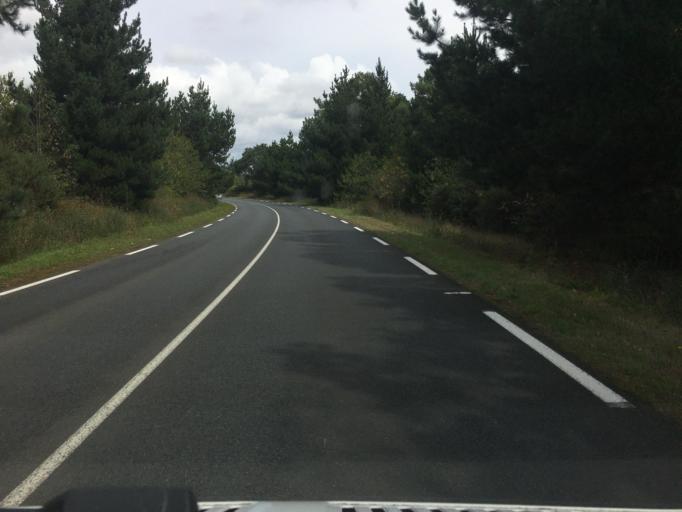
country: FR
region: Brittany
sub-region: Departement du Finistere
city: Plobannalec-Lesconil
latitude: 47.8517
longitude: -4.2099
